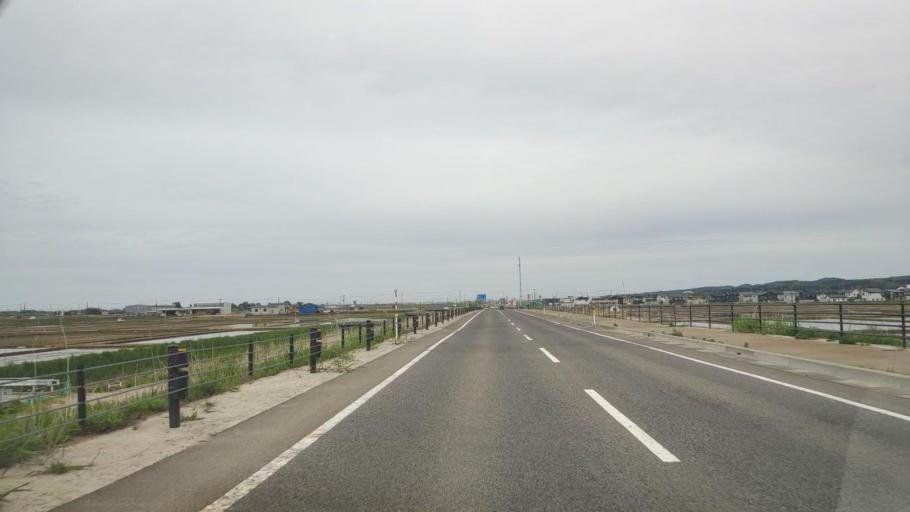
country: JP
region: Niigata
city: Niitsu-honcho
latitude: 37.7474
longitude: 139.0849
